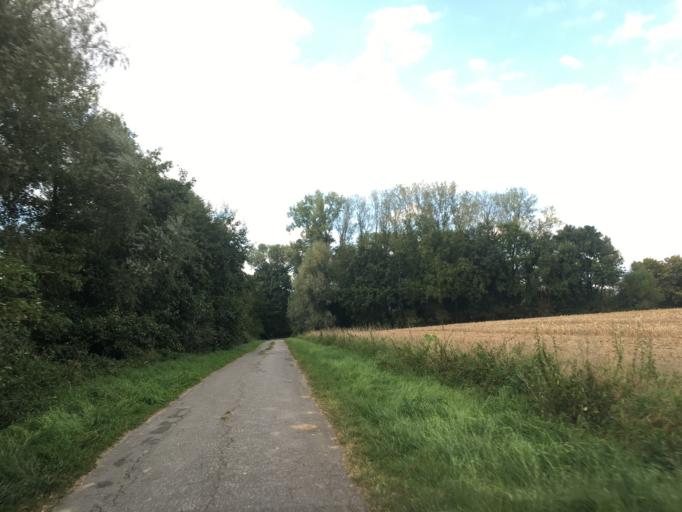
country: DE
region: North Rhine-Westphalia
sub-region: Regierungsbezirk Munster
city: Altenberge
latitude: 51.9827
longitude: 7.5193
